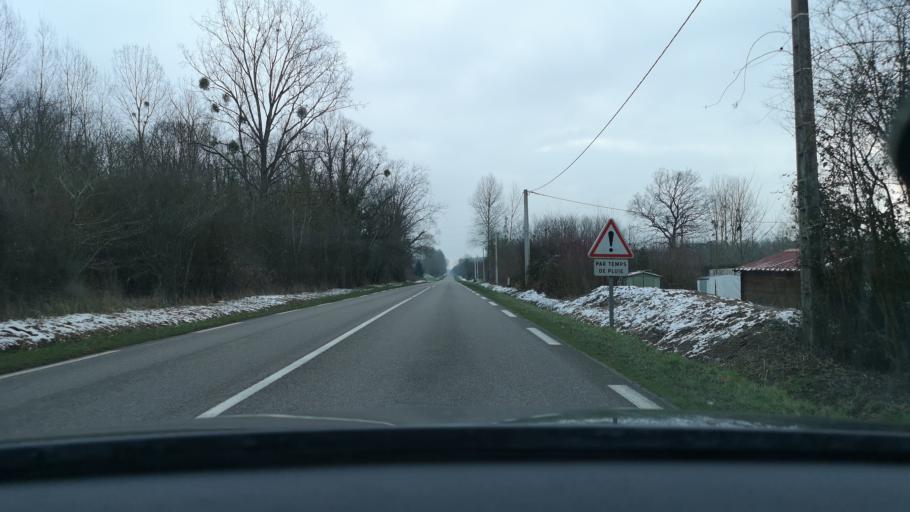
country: FR
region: Bourgogne
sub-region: Departement de Saone-et-Loire
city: Saint-Marcel
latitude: 46.7816
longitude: 4.9381
